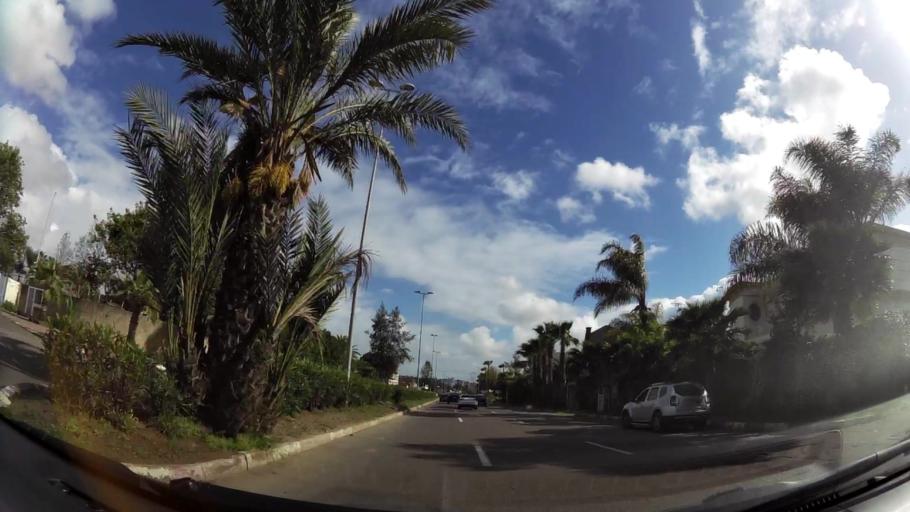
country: MA
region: Grand Casablanca
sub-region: Casablanca
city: Casablanca
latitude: 33.5412
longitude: -7.6185
